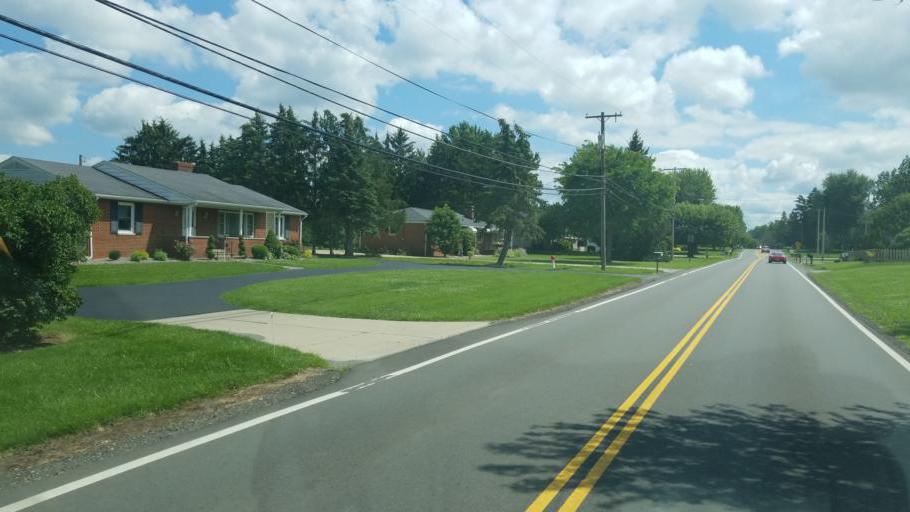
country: US
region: Ohio
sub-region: Richland County
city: Shelby
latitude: 40.8704
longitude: -82.6638
